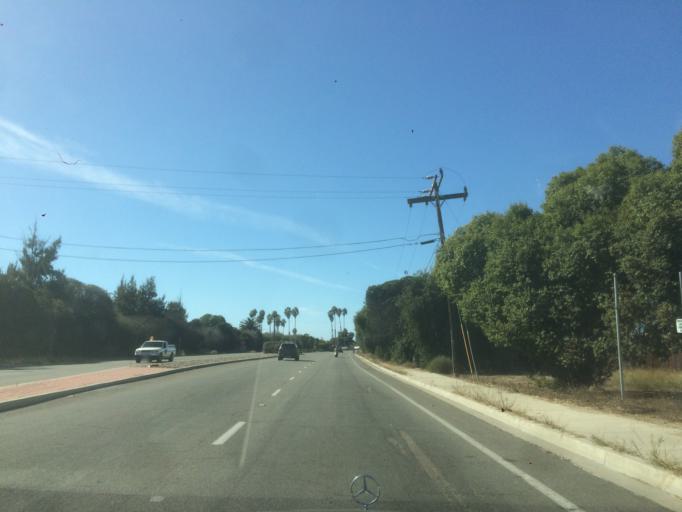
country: US
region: California
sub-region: Santa Barbara County
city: Goleta
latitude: 34.4357
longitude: -119.8319
